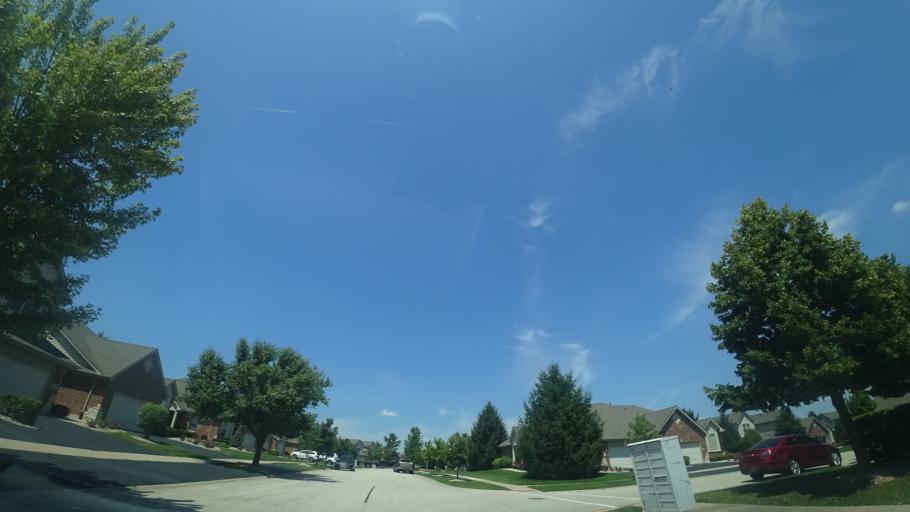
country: US
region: Illinois
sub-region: Will County
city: Mokena
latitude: 41.5597
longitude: -87.9042
